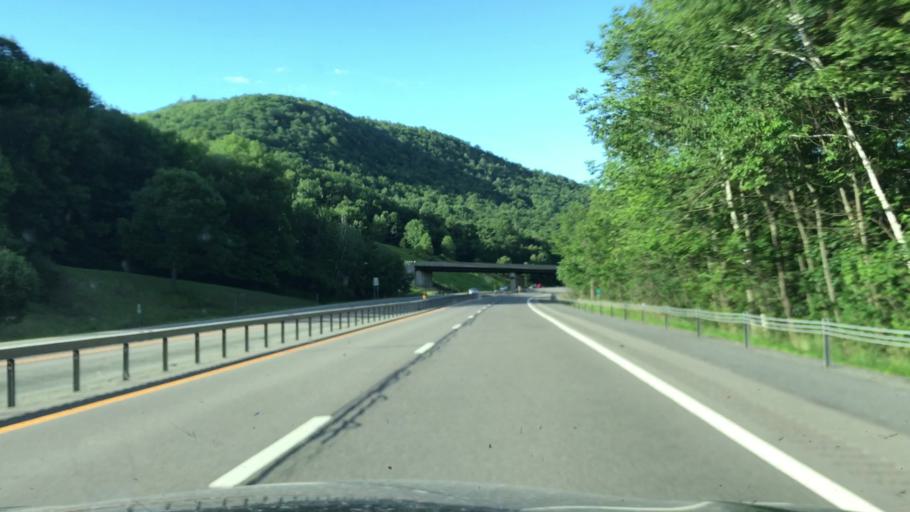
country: US
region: New York
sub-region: Delaware County
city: Hancock
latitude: 41.9632
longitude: -75.2325
